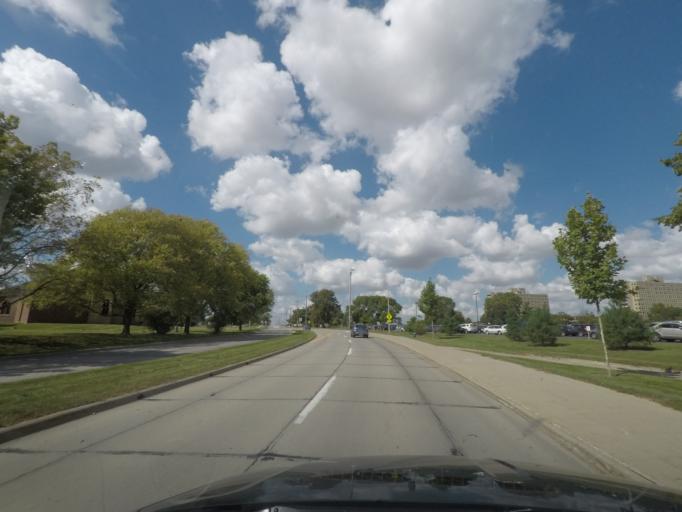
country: US
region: Iowa
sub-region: Story County
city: Ames
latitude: 42.0118
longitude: -93.6476
